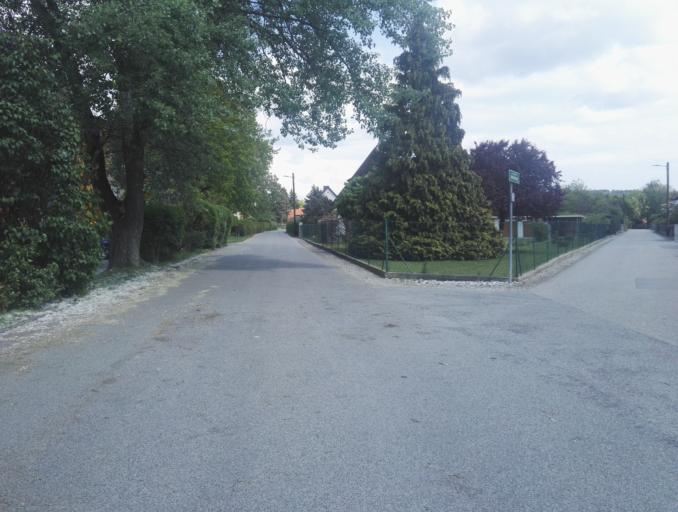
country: AT
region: Styria
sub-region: Politischer Bezirk Graz-Umgebung
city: Feldkirchen bei Graz
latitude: 47.0370
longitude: 15.4651
